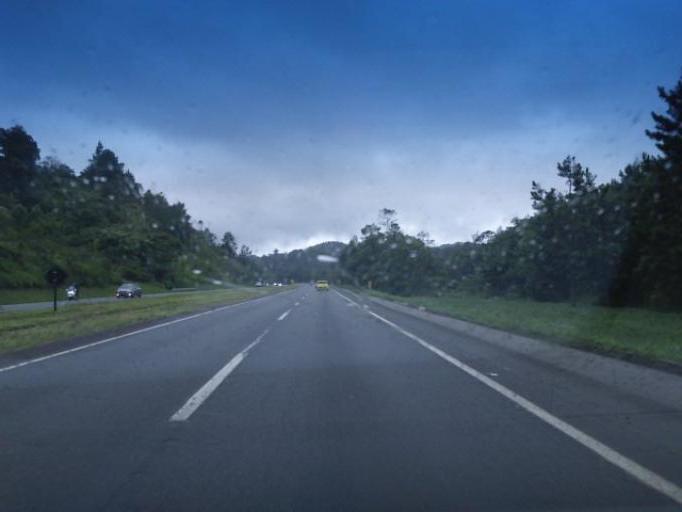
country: BR
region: Parana
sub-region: Antonina
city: Antonina
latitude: -25.0754
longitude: -48.5913
